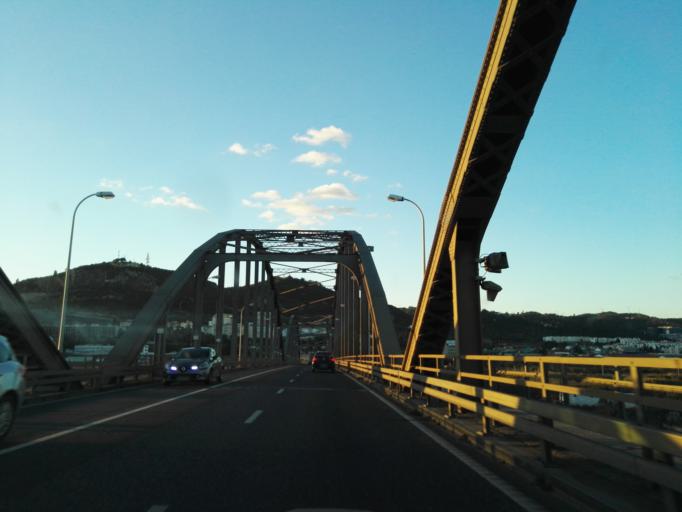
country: PT
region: Lisbon
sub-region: Vila Franca de Xira
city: Vila Franca de Xira
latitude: 38.9564
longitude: -8.9789
